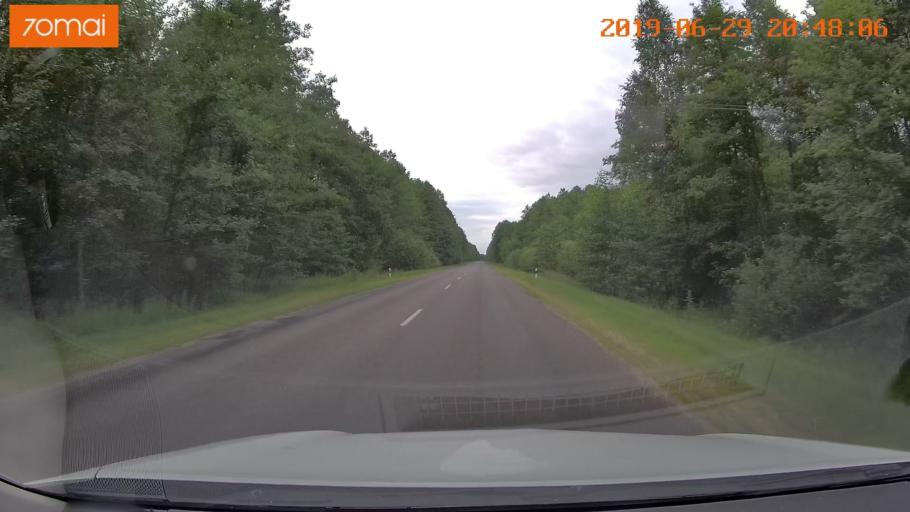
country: BY
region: Brest
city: Hantsavichy
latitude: 52.6461
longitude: 26.3169
